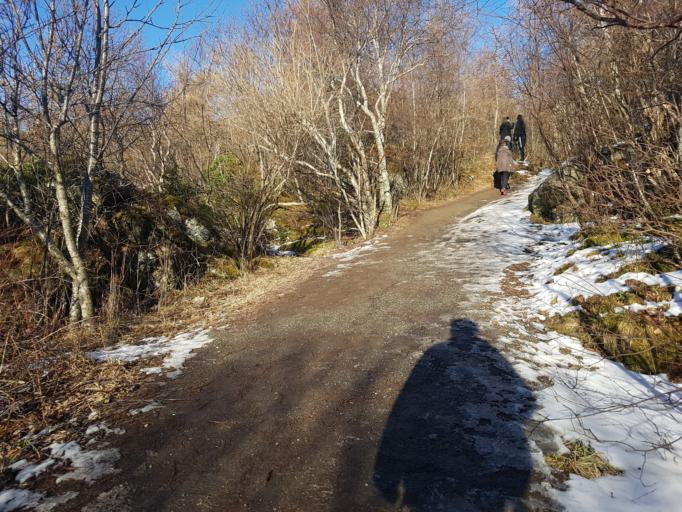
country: NO
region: Sor-Trondelag
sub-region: Trondheim
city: Trondheim
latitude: 63.4544
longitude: 10.4405
